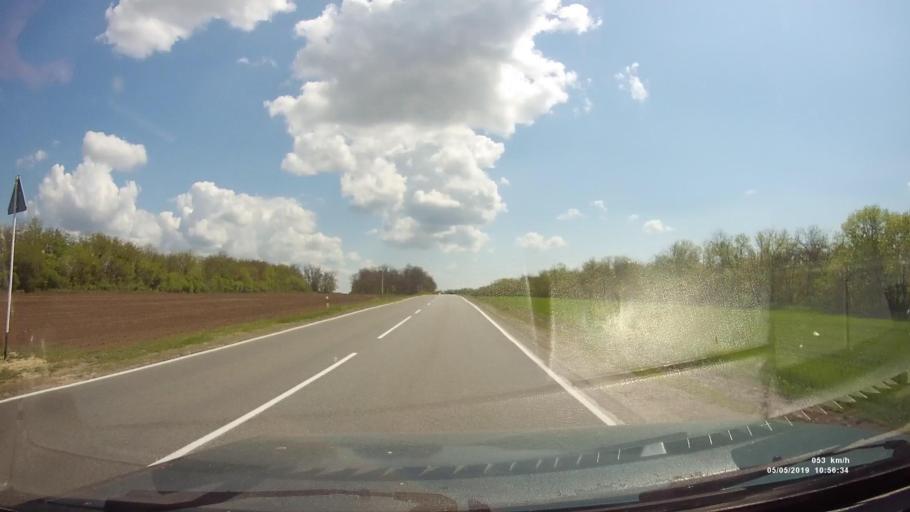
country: RU
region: Rostov
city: Ust'-Donetskiy
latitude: 47.6714
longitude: 40.8225
